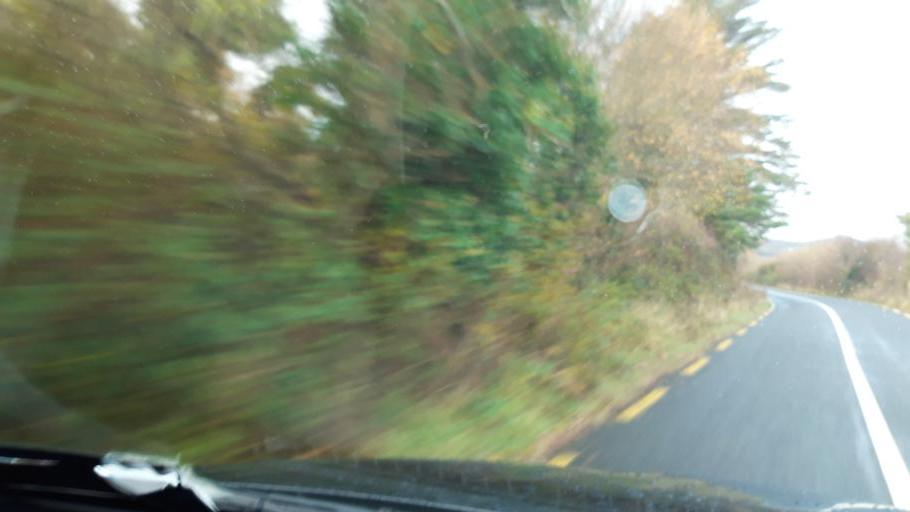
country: IE
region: Ulster
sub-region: County Donegal
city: Buncrana
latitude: 55.1621
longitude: -7.5673
